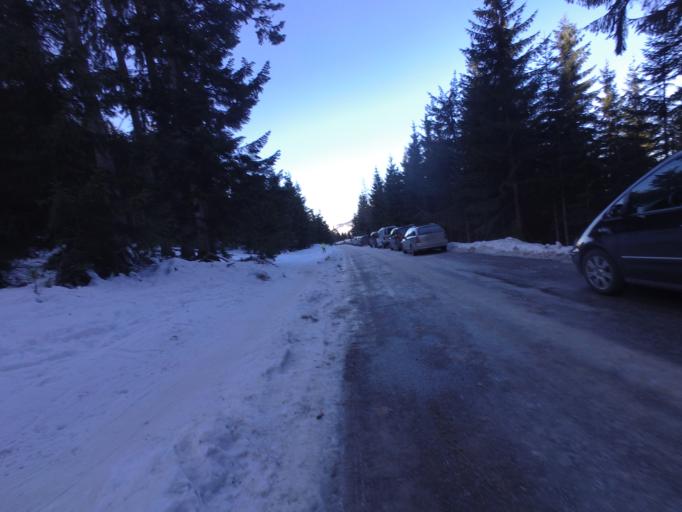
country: AT
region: Salzburg
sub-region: Politischer Bezirk Hallein
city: Scheffau am Tennengebirge
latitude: 47.6423
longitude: 13.2453
